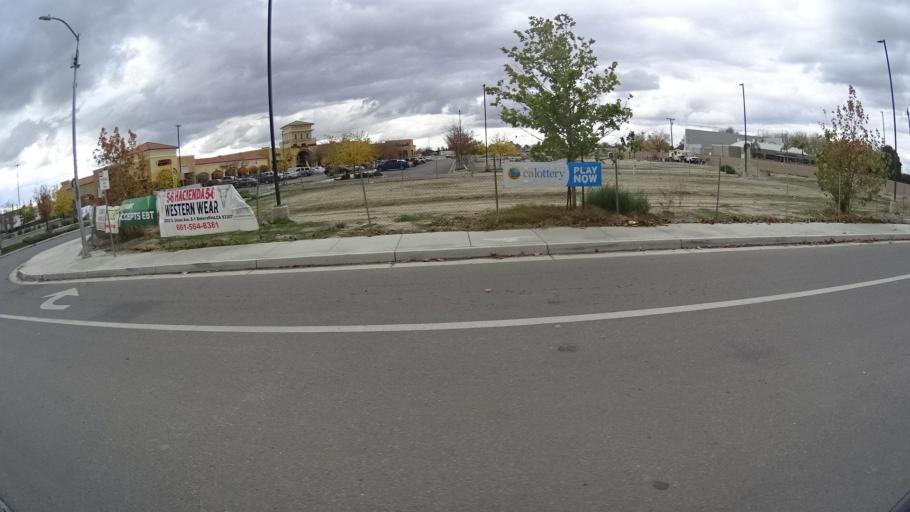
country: US
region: California
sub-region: Kern County
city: Greenfield
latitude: 35.3221
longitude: -119.0032
